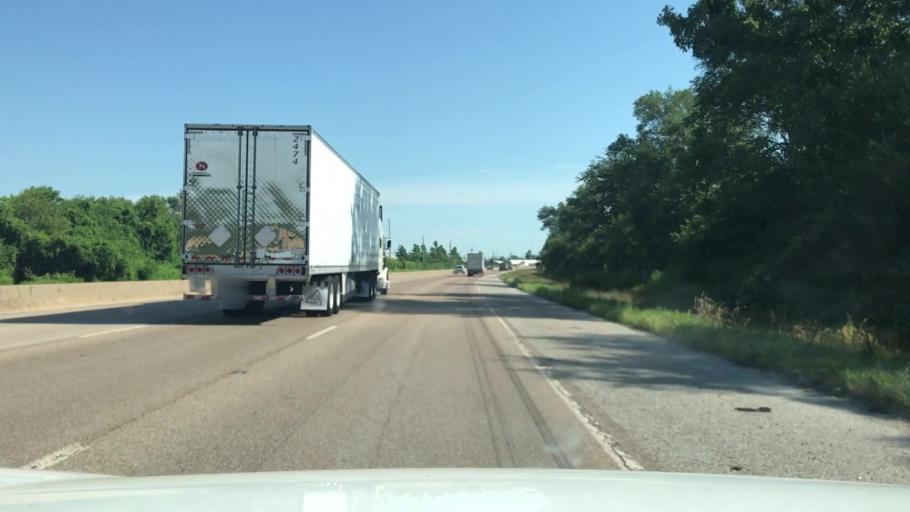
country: US
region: Illinois
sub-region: Madison County
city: Venice
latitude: 38.6830
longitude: -90.1729
